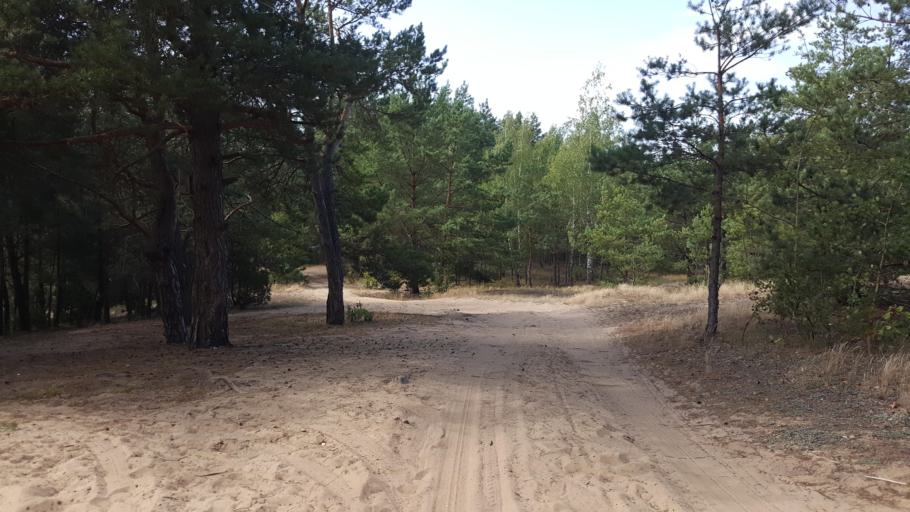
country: BY
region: Brest
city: Ivatsevichy
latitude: 52.7937
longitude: 25.5548
